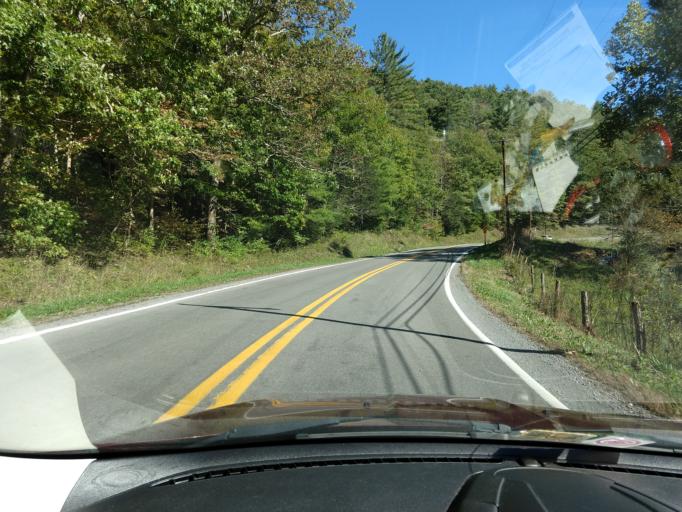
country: US
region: West Virginia
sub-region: Pocahontas County
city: Marlinton
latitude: 38.2127
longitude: -80.0397
